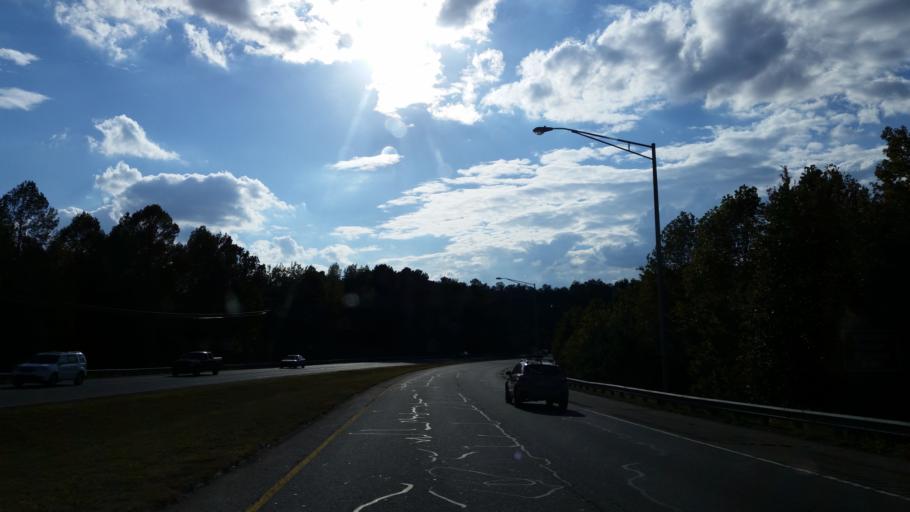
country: US
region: Georgia
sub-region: Bartow County
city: Cartersville
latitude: 34.1740
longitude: -84.7606
